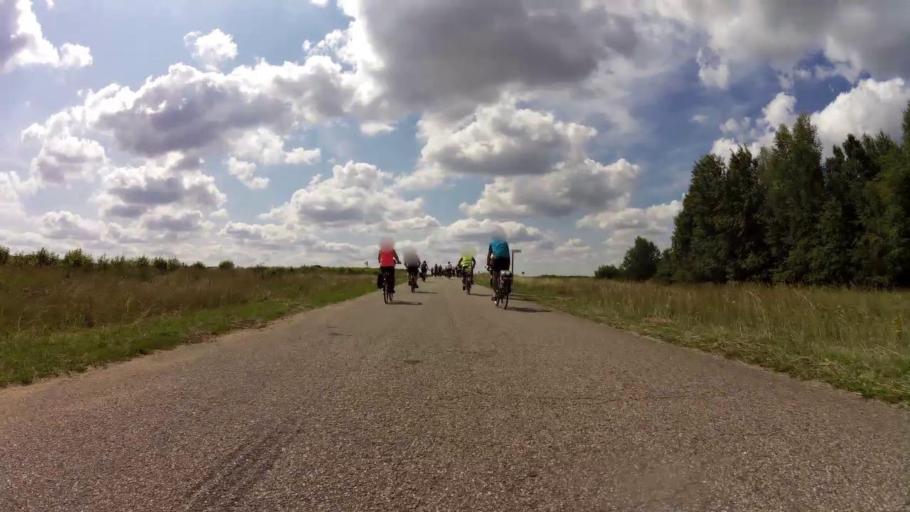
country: PL
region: West Pomeranian Voivodeship
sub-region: Powiat drawski
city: Drawsko Pomorskie
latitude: 53.4442
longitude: 15.7624
